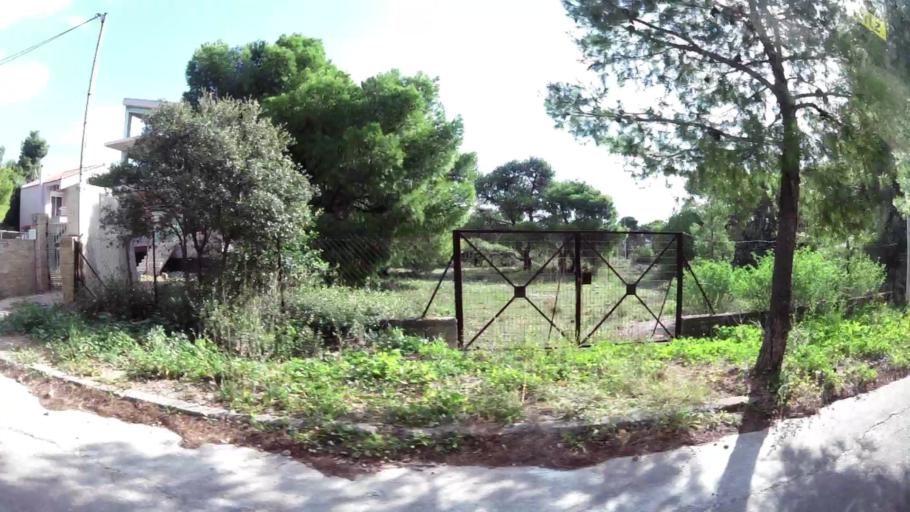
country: GR
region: Attica
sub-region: Nomarchia Anatolikis Attikis
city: Thrakomakedones
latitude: 38.1298
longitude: 23.7674
